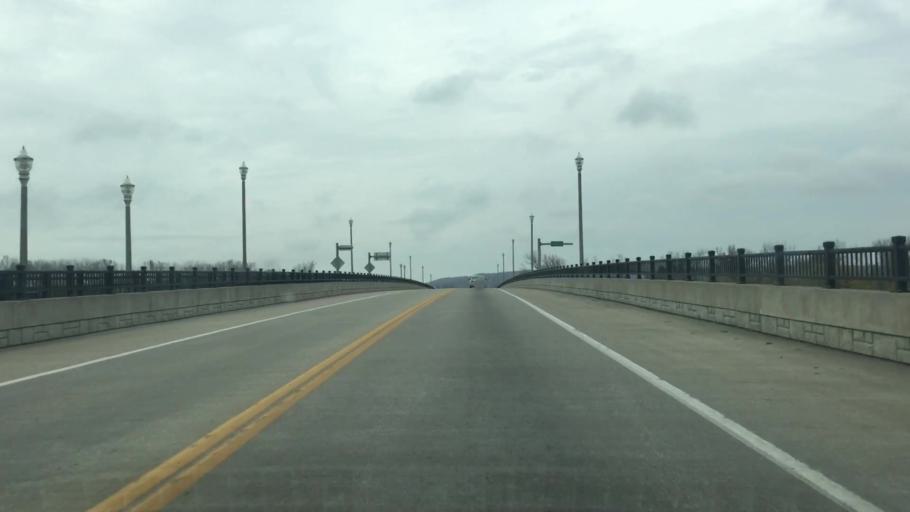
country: US
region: Missouri
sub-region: Gasconade County
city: Hermann
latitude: 38.7083
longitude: -91.4383
